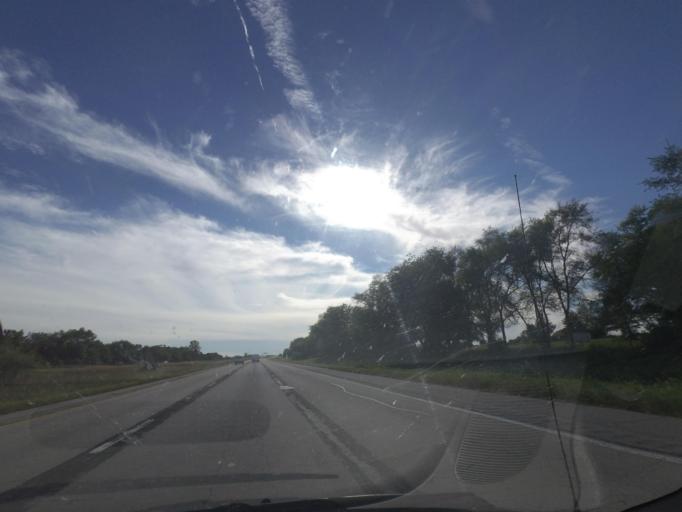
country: US
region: Illinois
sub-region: Macon County
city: Forsyth
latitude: 39.9018
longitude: -88.9972
